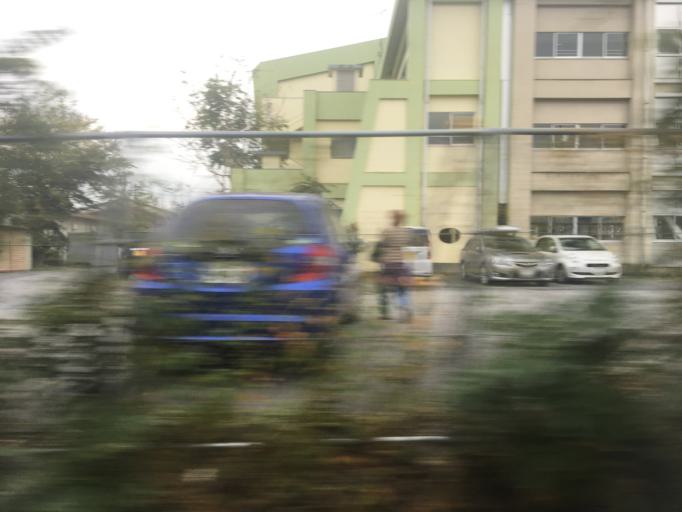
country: JP
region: Saitama
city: Sakado
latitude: 35.9126
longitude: 139.4222
